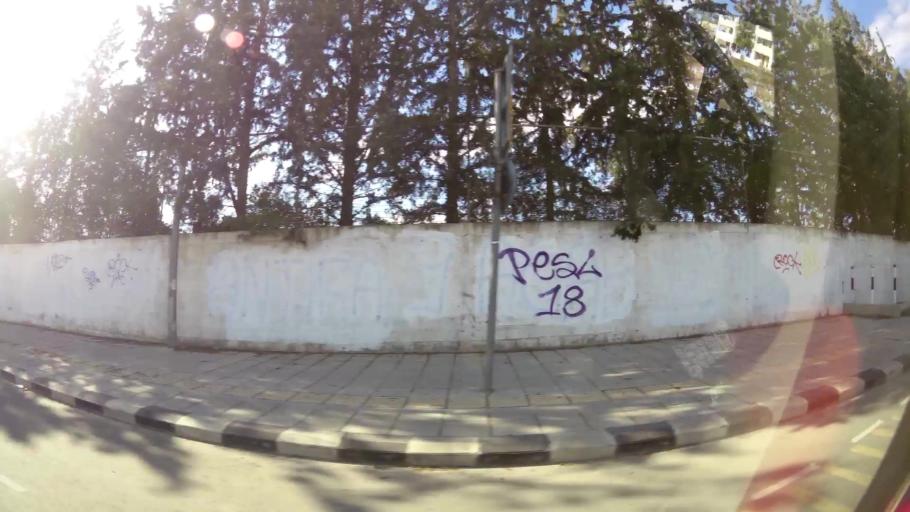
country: CY
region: Lefkosia
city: Nicosia
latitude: 35.1351
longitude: 33.3622
